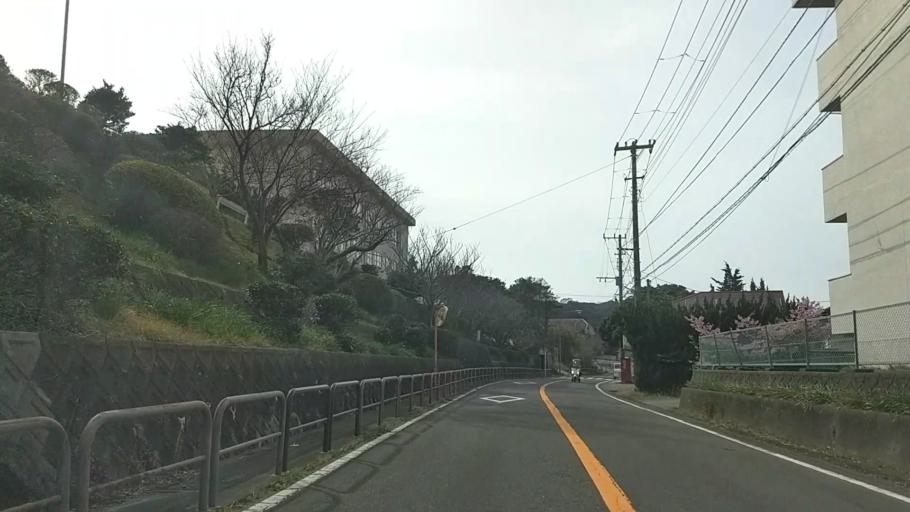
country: JP
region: Shizuoka
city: Shimoda
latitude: 34.6691
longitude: 138.9636
